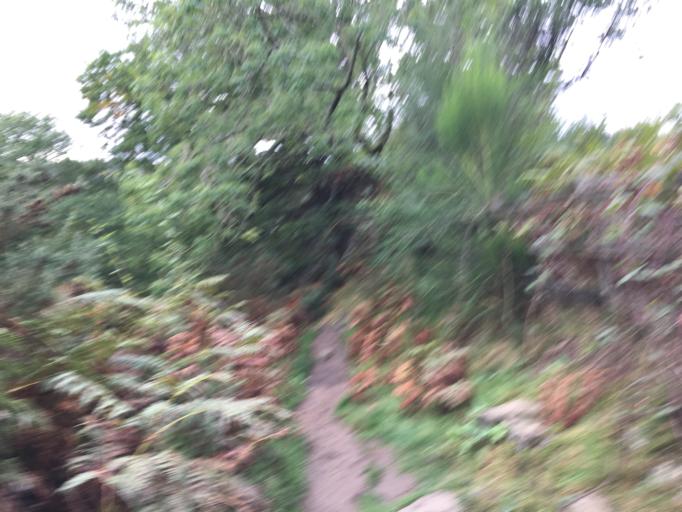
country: GB
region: England
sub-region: North Yorkshire
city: Sleights
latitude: 54.4095
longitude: -0.7340
